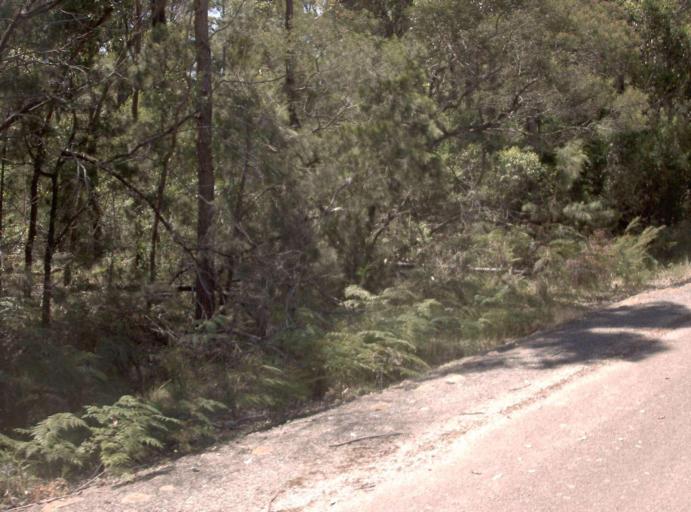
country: AU
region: Victoria
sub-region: East Gippsland
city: Lakes Entrance
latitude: -37.7530
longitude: 148.3330
